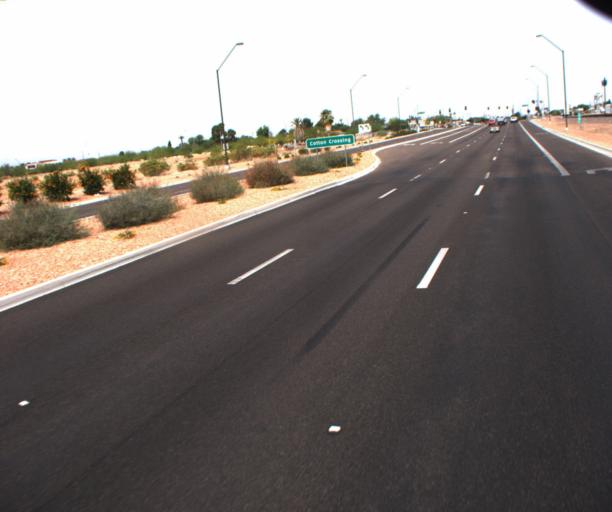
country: US
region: Arizona
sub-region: Maricopa County
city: Peoria
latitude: 33.5763
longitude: -112.2314
